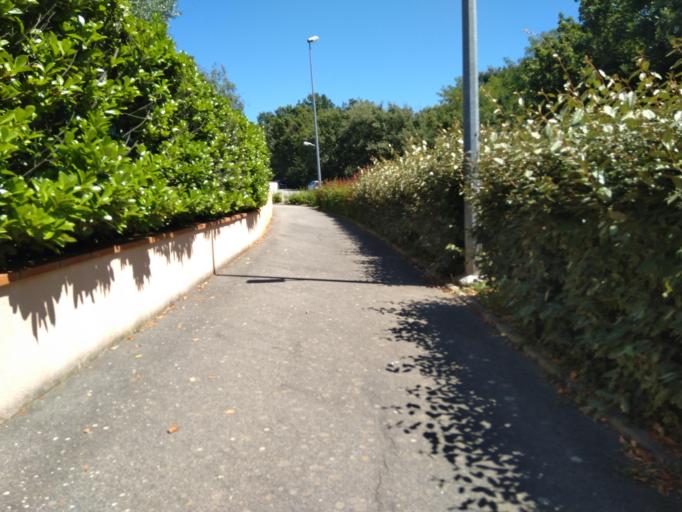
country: FR
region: Midi-Pyrenees
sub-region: Departement de la Haute-Garonne
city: Labege
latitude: 43.5367
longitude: 1.5362
